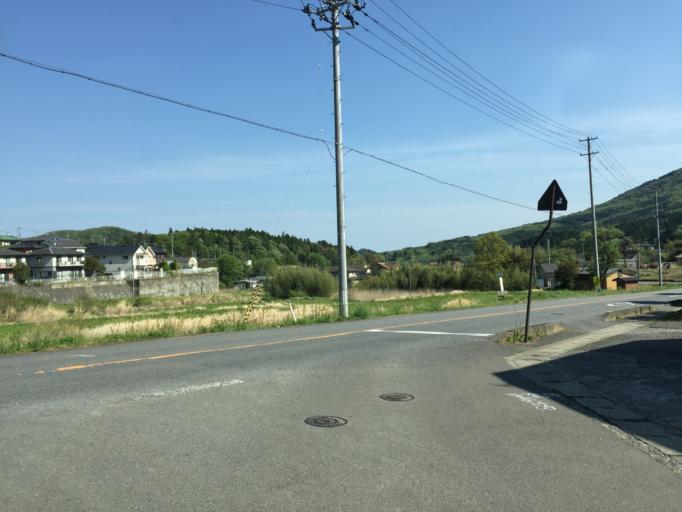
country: JP
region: Fukushima
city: Iwaki
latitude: 37.0520
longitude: 140.7950
